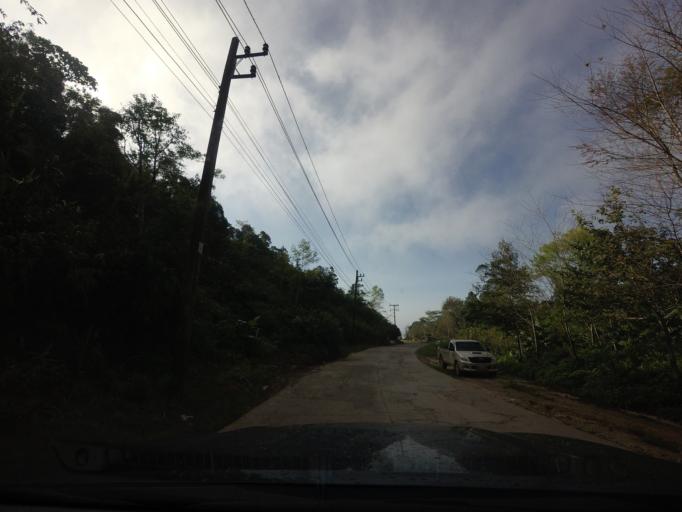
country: TH
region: Phetchabun
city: Lom Kao
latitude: 16.8959
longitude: 101.1043
